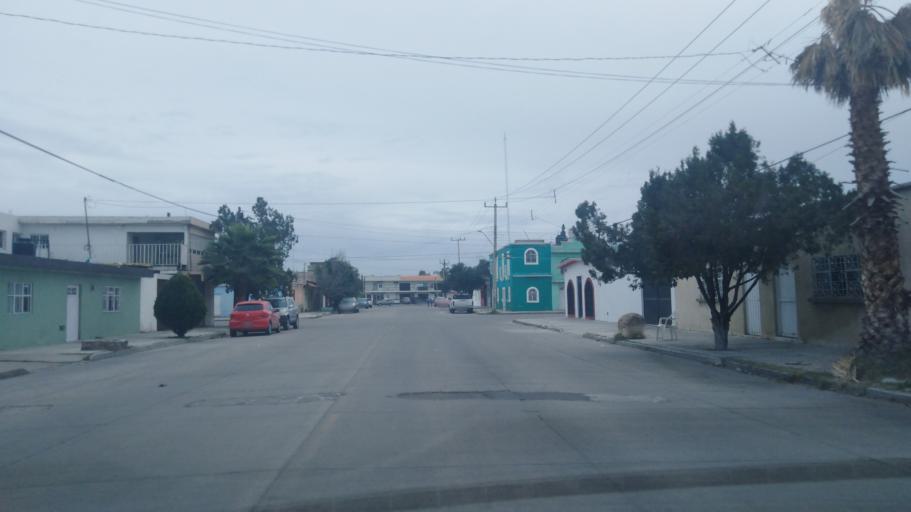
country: MX
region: Durango
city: Victoria de Durango
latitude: 24.0285
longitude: -104.6264
